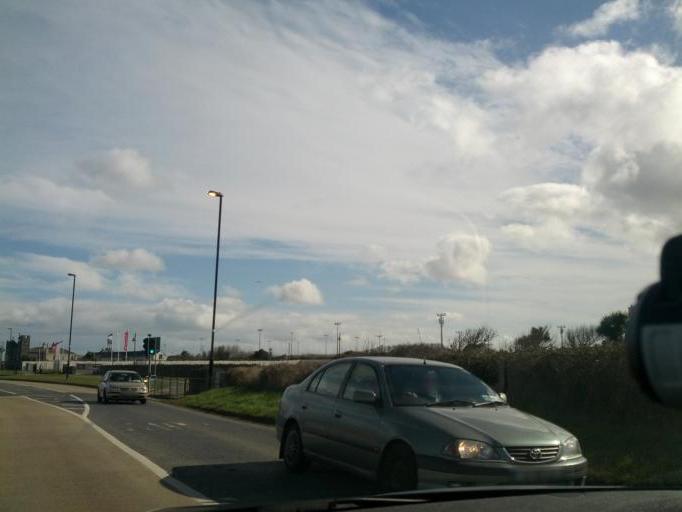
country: IE
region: Leinster
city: Portmarnock
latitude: 53.4458
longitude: -6.1309
